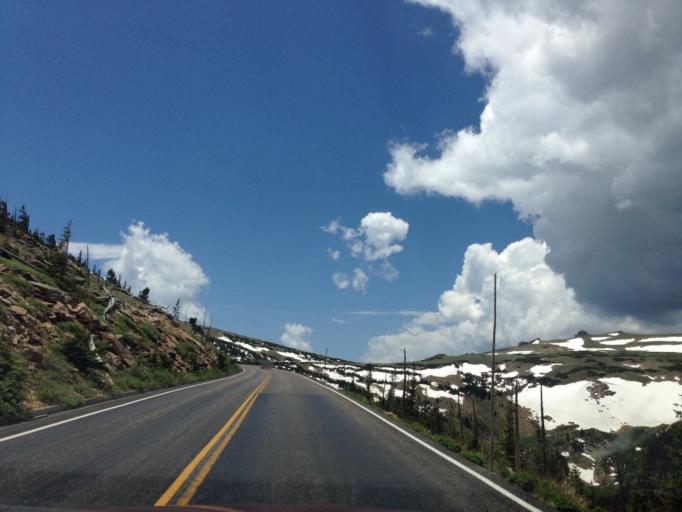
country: US
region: Colorado
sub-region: Larimer County
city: Estes Park
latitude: 40.3969
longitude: -105.6773
